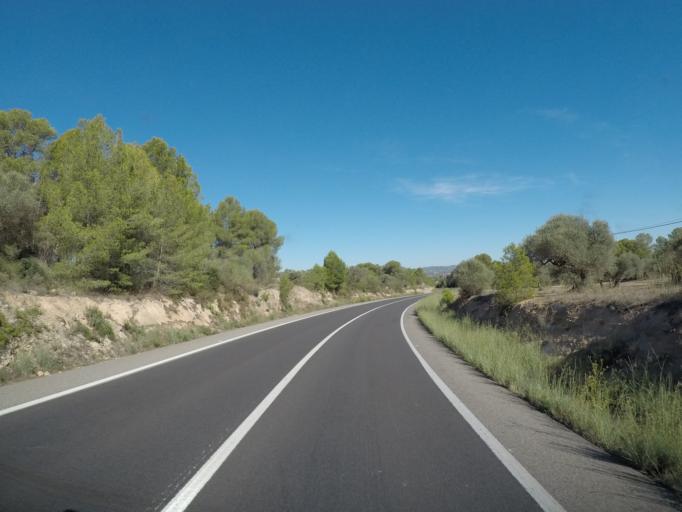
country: ES
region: Catalonia
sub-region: Provincia de Tarragona
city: Rasquera
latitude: 41.0184
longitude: 0.6085
